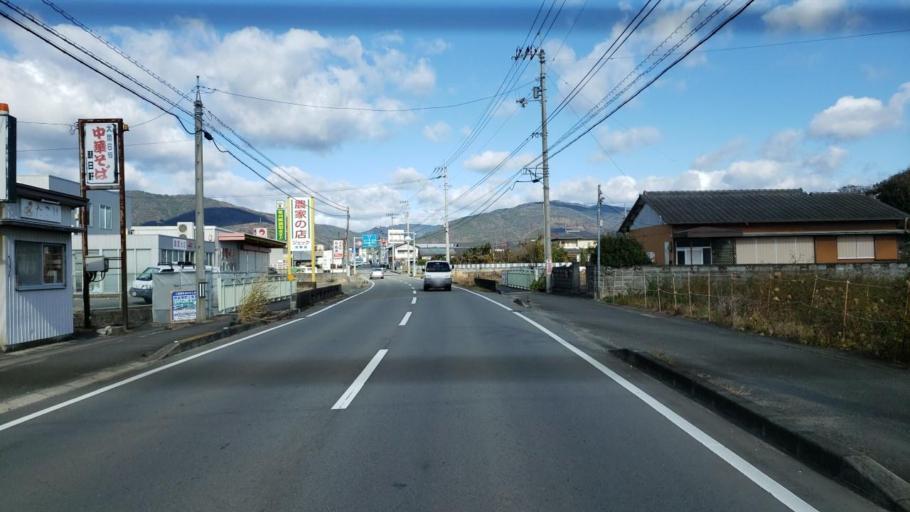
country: JP
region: Tokushima
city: Kamojimacho-jogejima
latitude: 34.0984
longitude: 134.3449
